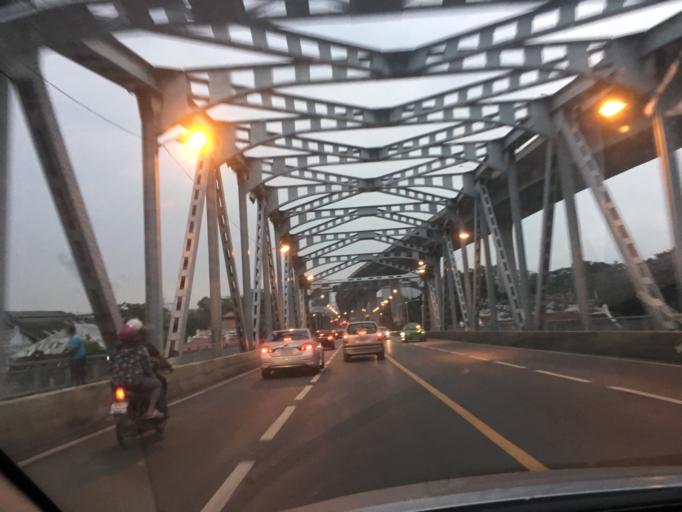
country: TH
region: Bangkok
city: Bang Kho Laem
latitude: 13.7014
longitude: 100.4912
